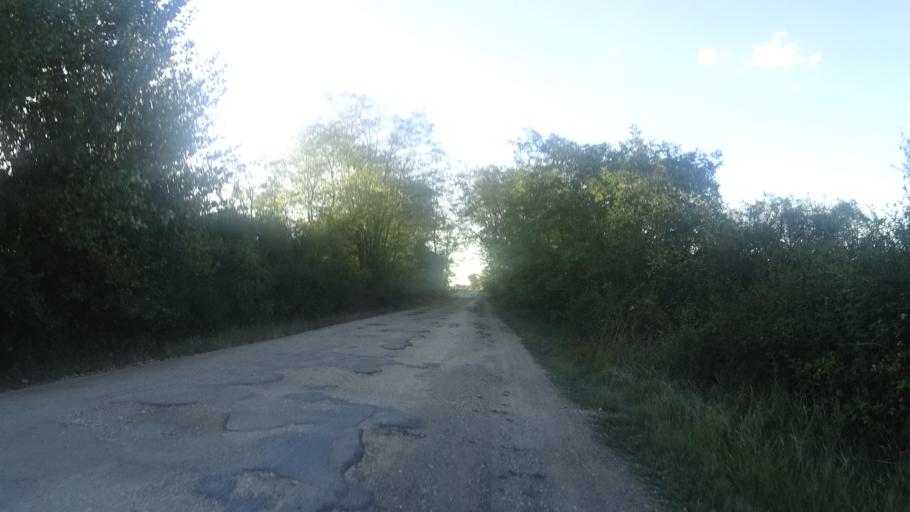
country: FR
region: Centre
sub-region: Departement du Cher
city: Cuffy
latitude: 46.9640
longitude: 3.0648
